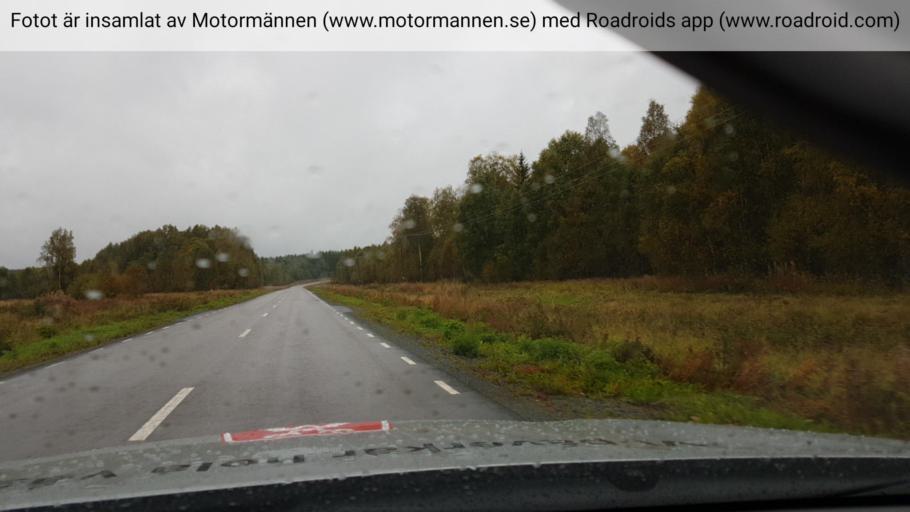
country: SE
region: Norrbotten
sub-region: Lulea Kommun
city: Sodra Sunderbyn
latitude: 65.8229
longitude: 21.9237
